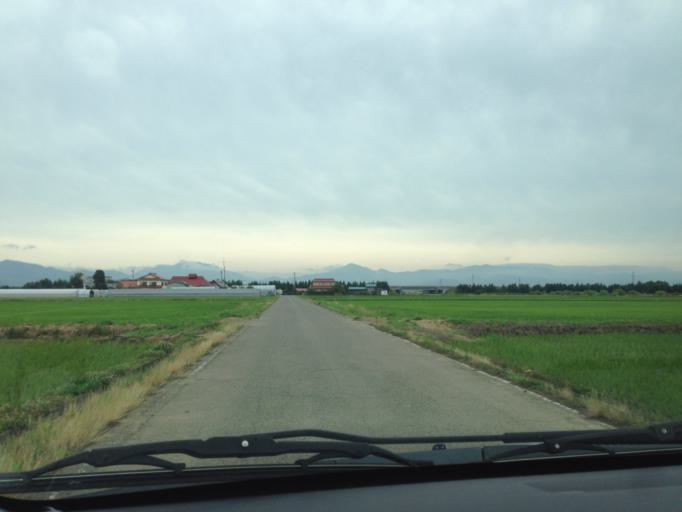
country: JP
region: Fukushima
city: Kitakata
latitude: 37.5394
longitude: 139.8880
